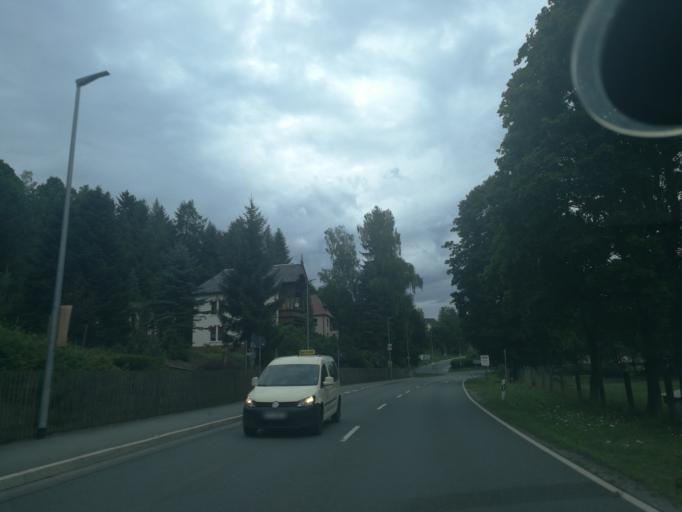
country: DE
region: Saxony
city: Adorf
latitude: 50.3109
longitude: 12.2524
